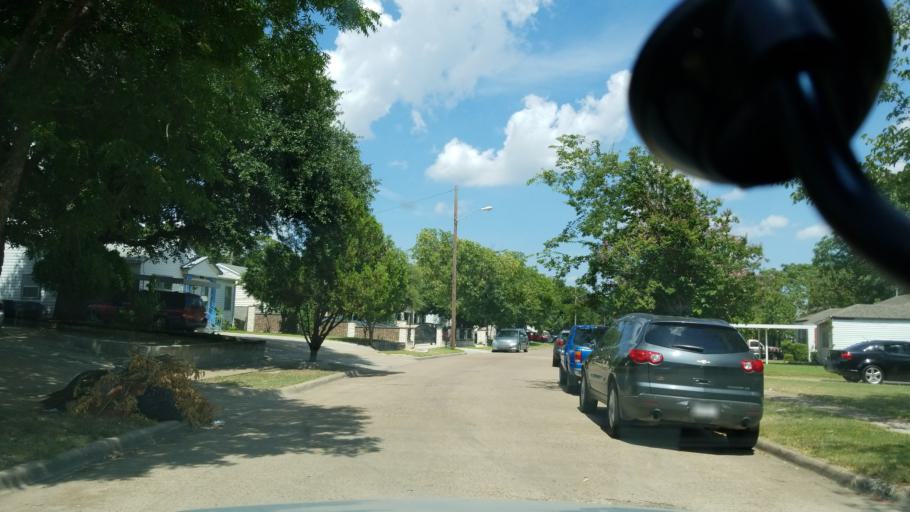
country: US
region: Texas
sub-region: Dallas County
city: Cockrell Hill
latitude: 32.7247
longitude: -96.8807
